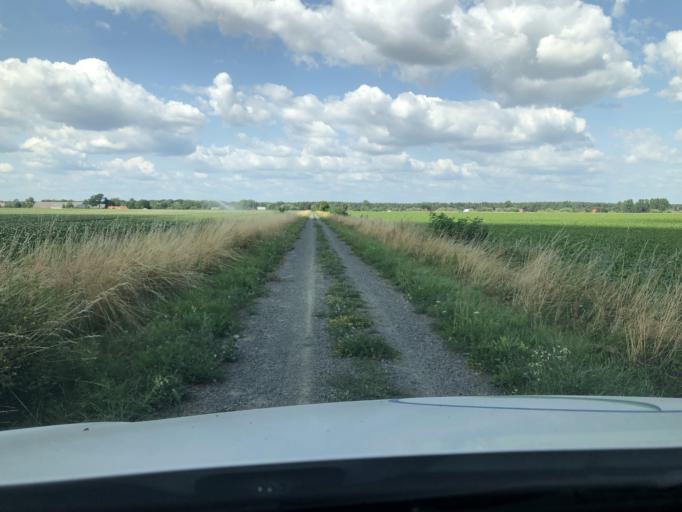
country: SE
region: Skane
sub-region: Kristianstads Kommun
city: Degeberga
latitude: 55.8888
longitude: 14.0809
